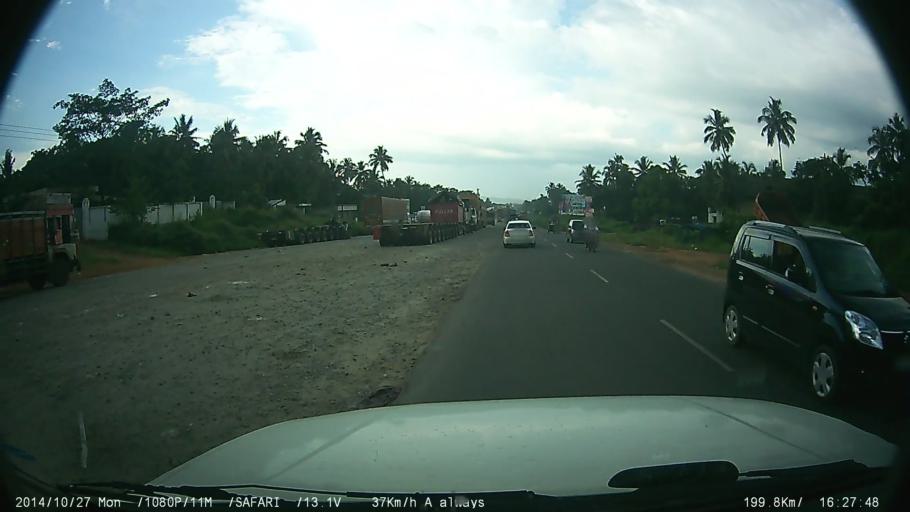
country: IN
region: Kerala
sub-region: Thrissur District
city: Trichur
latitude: 10.5174
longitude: 76.2587
